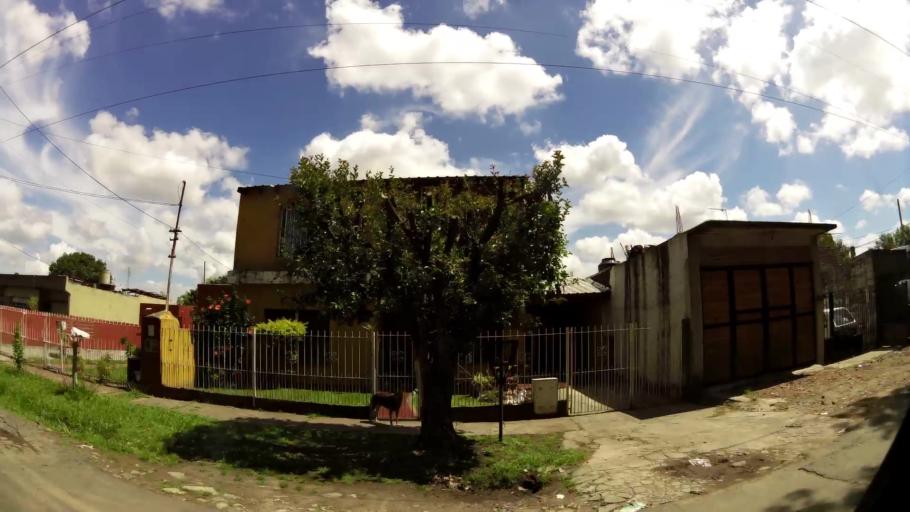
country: AR
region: Buenos Aires
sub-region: Partido de Quilmes
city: Quilmes
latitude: -34.8085
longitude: -58.2567
